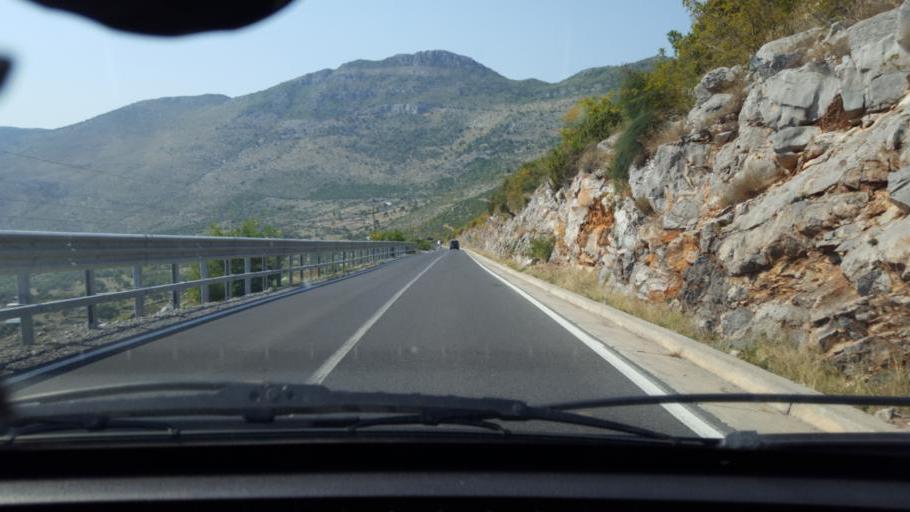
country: AL
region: Shkoder
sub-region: Rrethi i Malesia e Madhe
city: Hot
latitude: 42.3743
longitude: 19.4573
